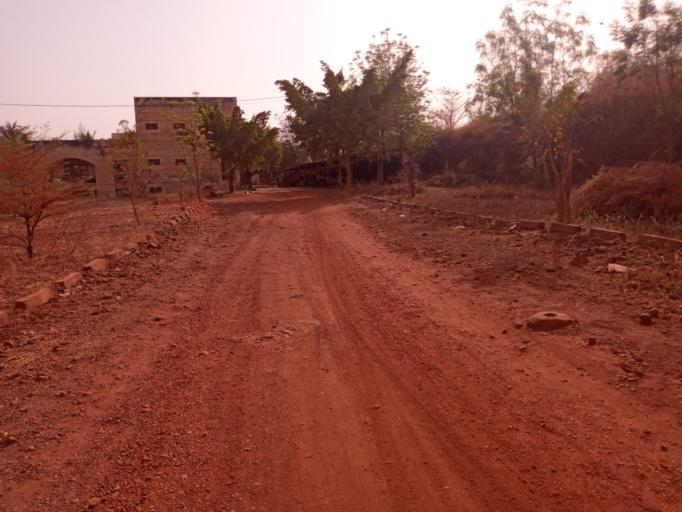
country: ML
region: Bamako
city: Bamako
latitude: 12.6128
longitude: -7.9908
